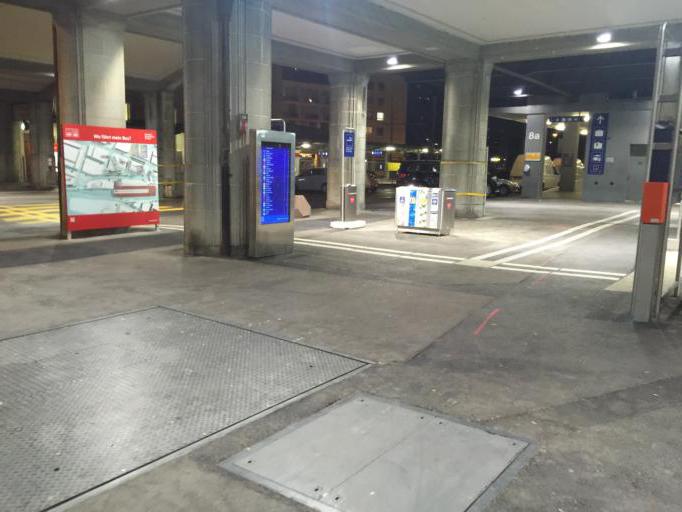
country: CH
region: Saint Gallen
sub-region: Wahlkreis St. Gallen
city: Sankt Gallen
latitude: 47.4227
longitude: 9.3687
